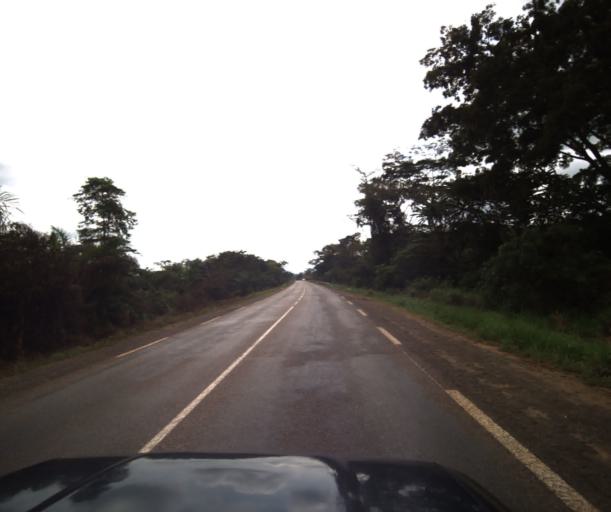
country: CM
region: Centre
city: Eseka
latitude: 3.8487
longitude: 10.4977
